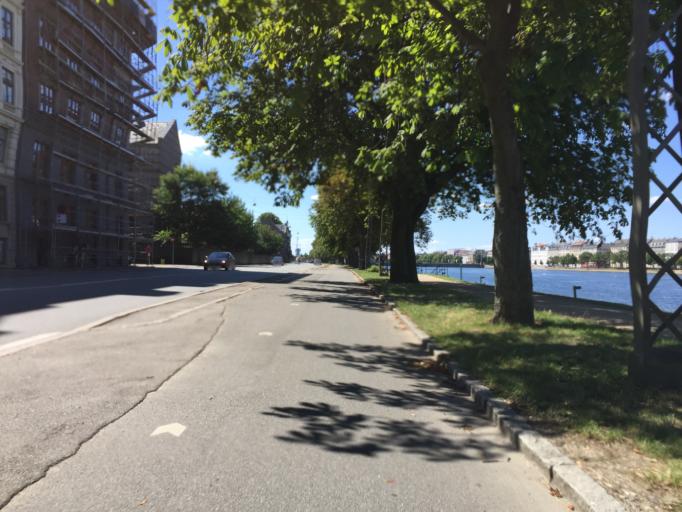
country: DK
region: Capital Region
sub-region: Kobenhavn
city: Copenhagen
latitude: 55.6901
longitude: 12.5705
